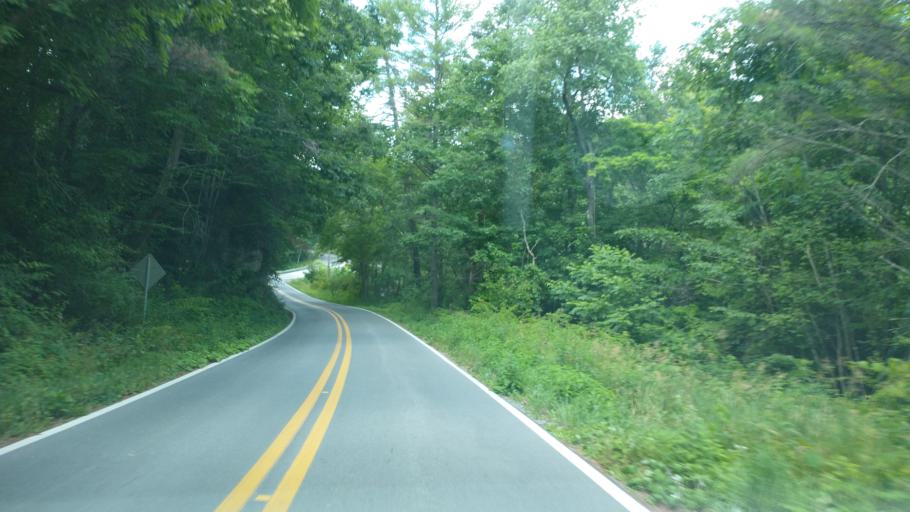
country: US
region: West Virginia
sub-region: Mercer County
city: Athens
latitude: 37.4339
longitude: -81.0611
